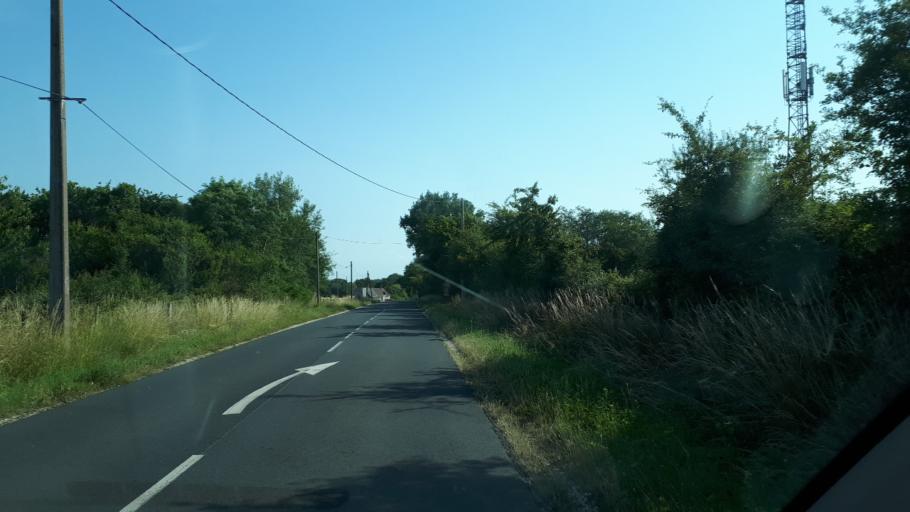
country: FR
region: Centre
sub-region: Departement du Loir-et-Cher
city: Droue
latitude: 47.9949
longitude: 1.0393
